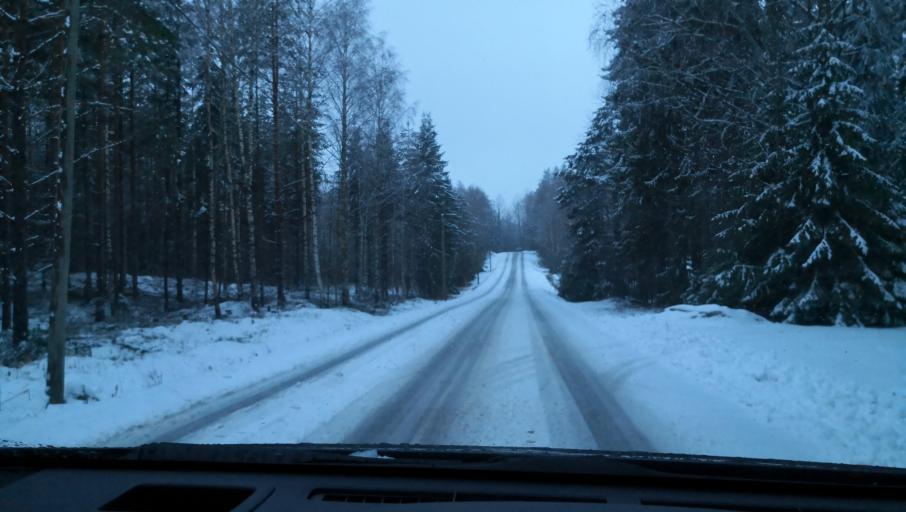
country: SE
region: Vaestmanland
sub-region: Kopings Kommun
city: Kolsva
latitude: 59.5926
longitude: 15.8169
